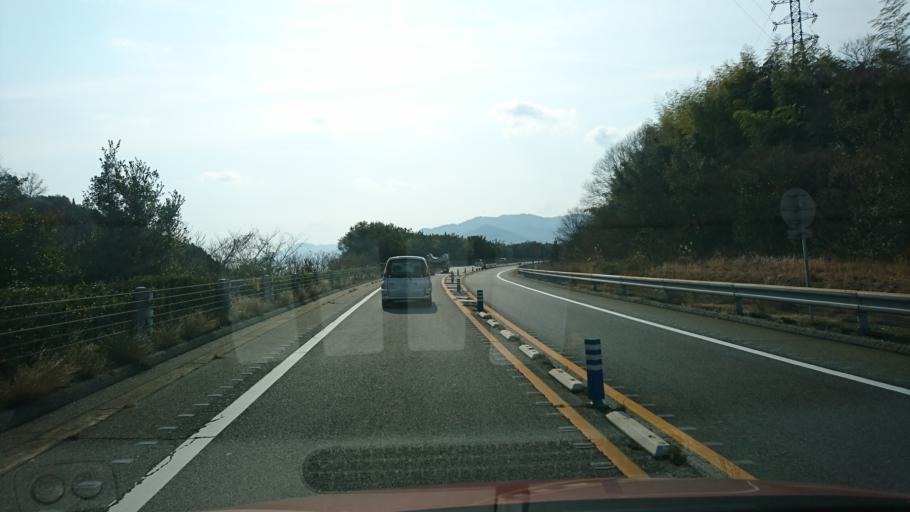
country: JP
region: Hiroshima
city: Onomichi
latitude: 34.3648
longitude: 133.1920
